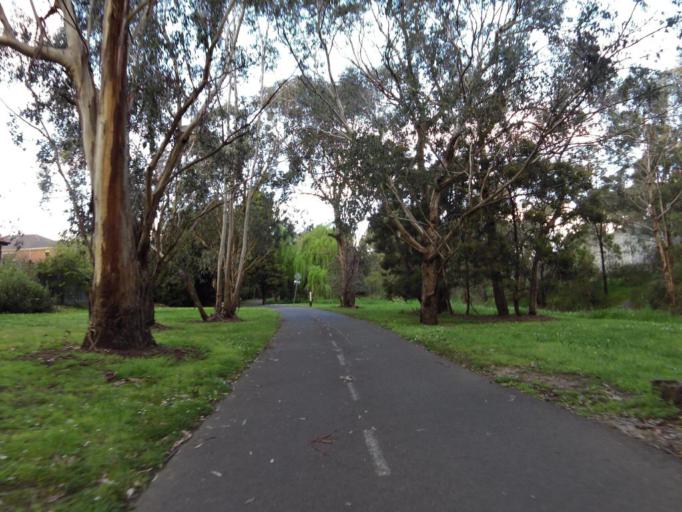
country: AU
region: Victoria
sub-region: Whitehorse
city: Blackburn North
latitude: -37.8019
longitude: 145.1649
